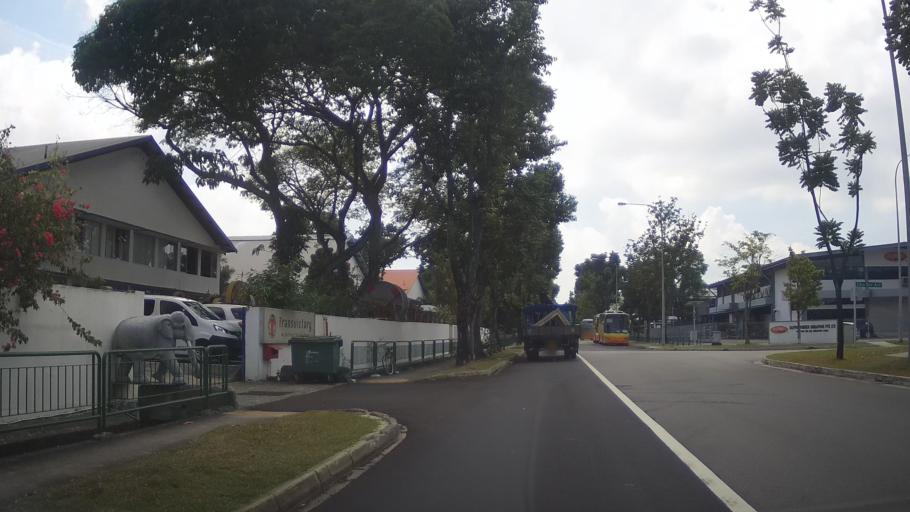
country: MY
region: Johor
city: Johor Bahru
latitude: 1.3348
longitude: 103.7154
